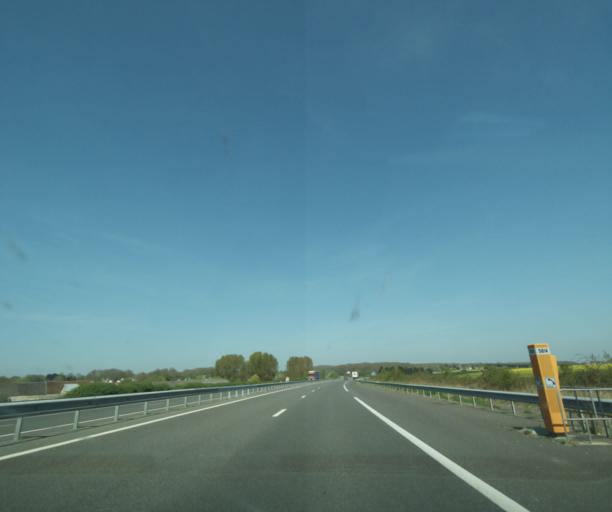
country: FR
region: Bourgogne
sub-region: Departement de la Nievre
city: Pouilly-sur-Loire
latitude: 47.3311
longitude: 2.9302
